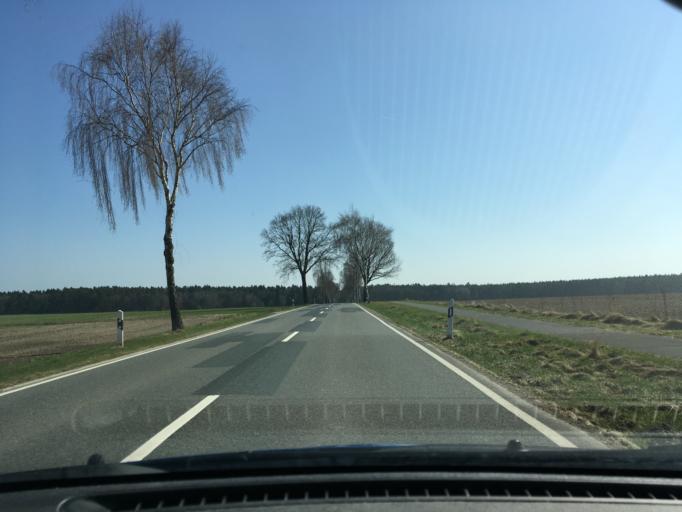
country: DE
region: Lower Saxony
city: Rehlingen
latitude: 53.0968
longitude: 10.2616
